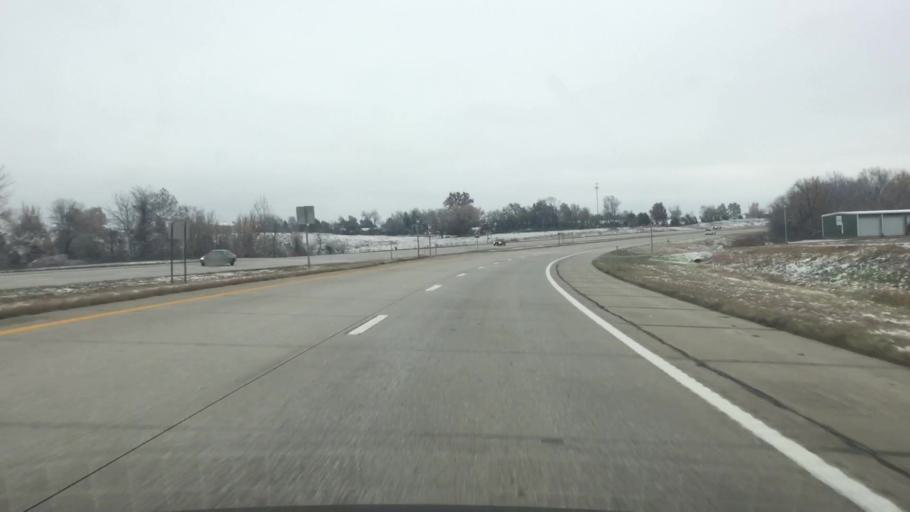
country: US
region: Missouri
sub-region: Saint Clair County
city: Osceola
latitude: 38.1767
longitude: -93.7230
